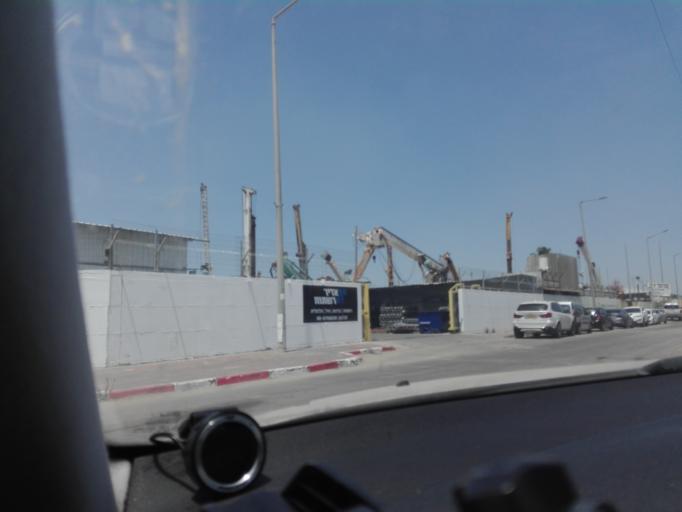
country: IL
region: Central District
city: Bene 'Ayish
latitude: 31.7350
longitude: 34.7567
